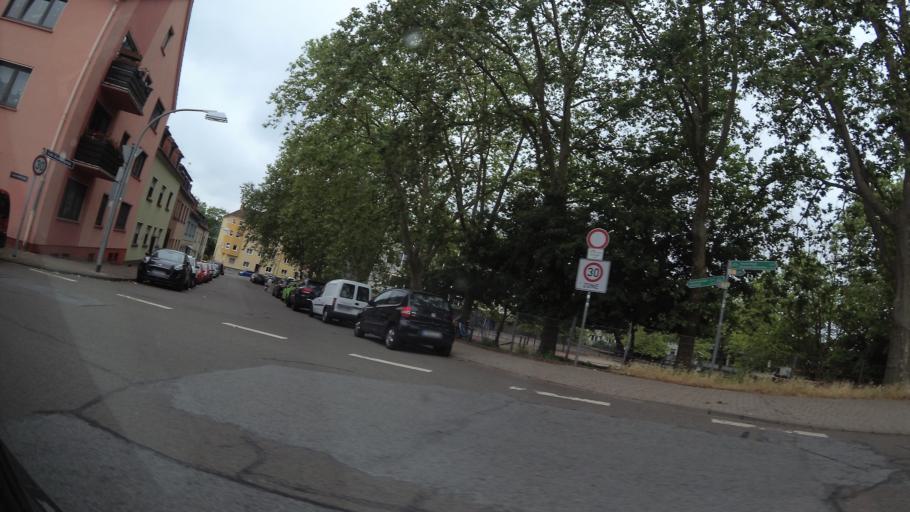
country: DE
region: Saarland
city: Saarbrucken
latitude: 49.2435
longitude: 6.9486
